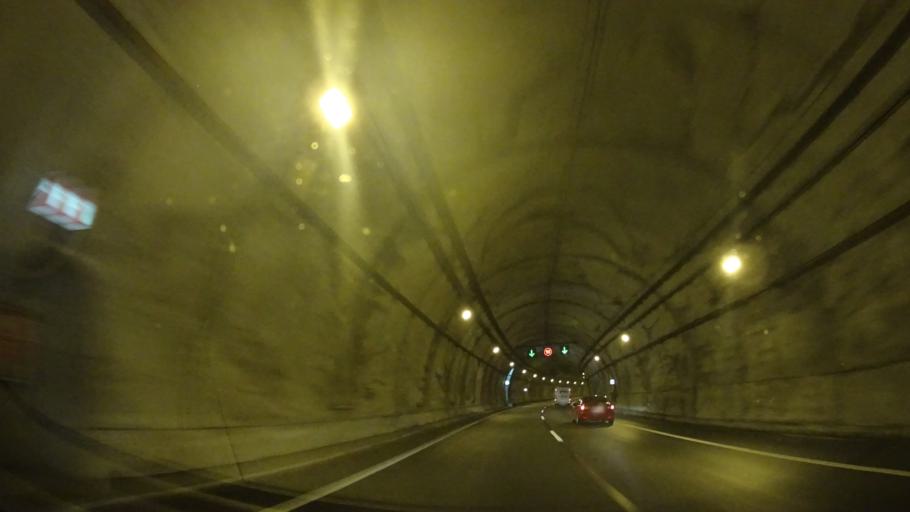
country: ES
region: Asturias
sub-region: Province of Asturias
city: Arriba
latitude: 43.4640
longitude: -5.5164
